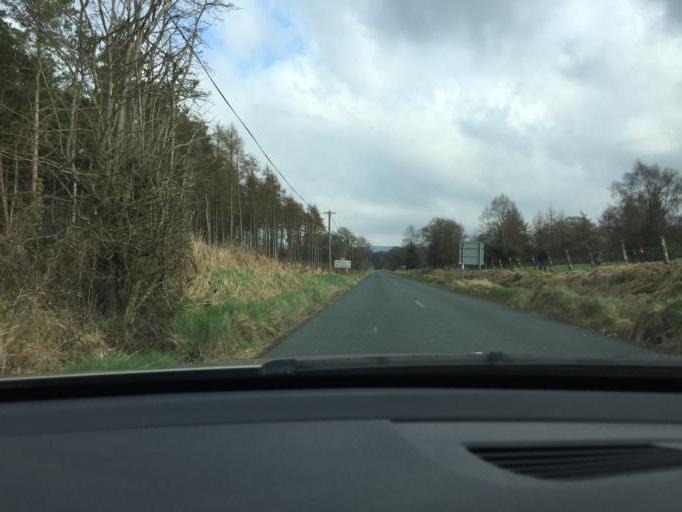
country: IE
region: Leinster
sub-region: Wicklow
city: Blessington
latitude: 53.1508
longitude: -6.5536
